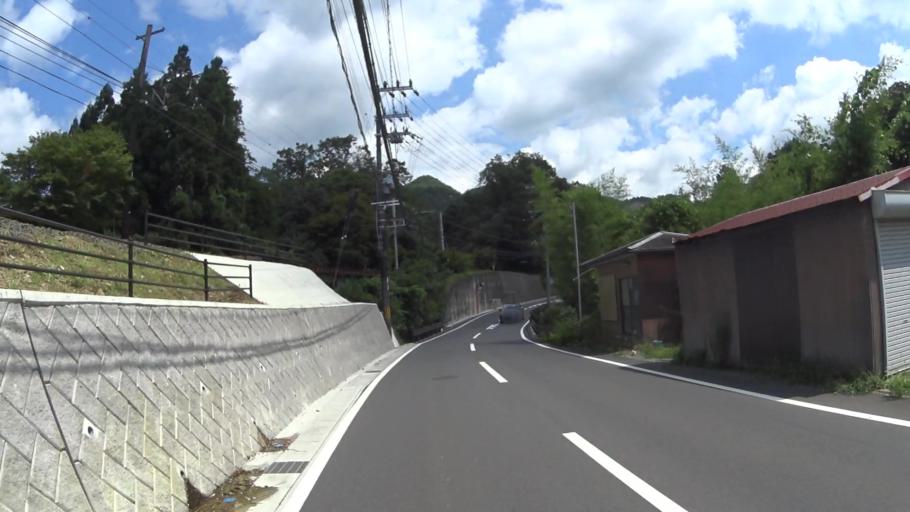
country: JP
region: Kyoto
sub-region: Kyoto-shi
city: Kamigyo-ku
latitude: 35.0918
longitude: 135.7658
